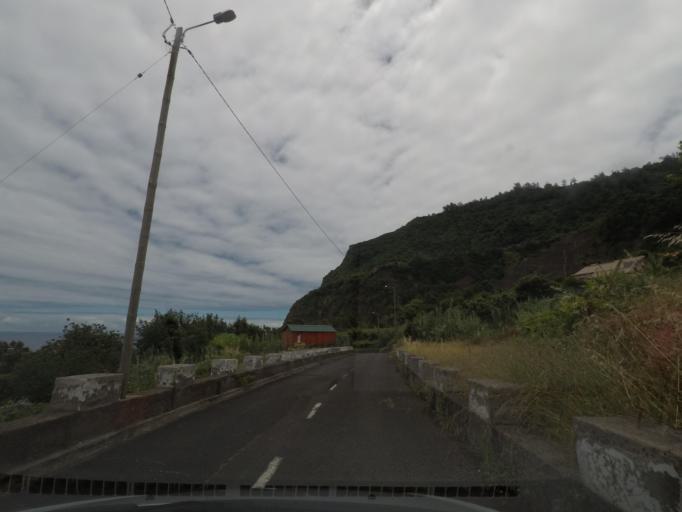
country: PT
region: Madeira
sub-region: Santana
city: Santana
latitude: 32.8273
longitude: -16.9511
